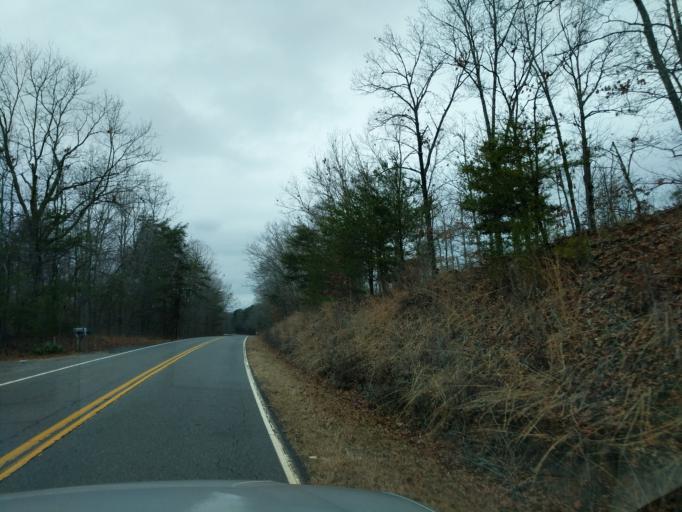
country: US
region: South Carolina
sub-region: Oconee County
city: Walhalla
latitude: 34.7940
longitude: -83.1692
